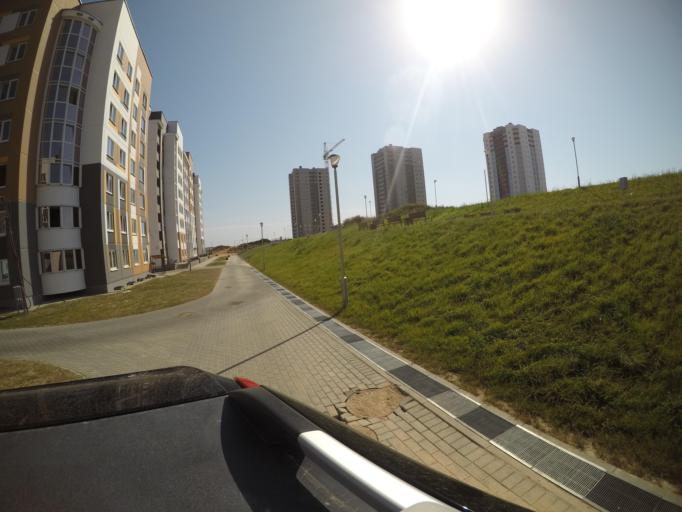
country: BY
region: Grodnenskaya
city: Hrodna
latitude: 53.7211
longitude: 23.8811
